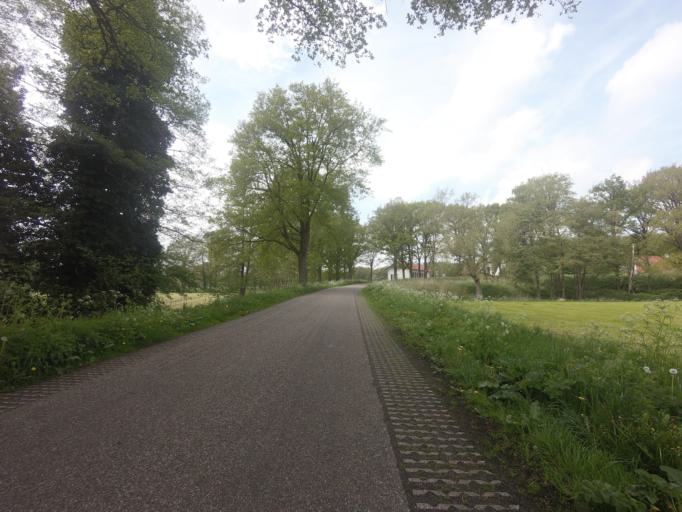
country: NL
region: Overijssel
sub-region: Gemeente Hof van Twente
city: Delden
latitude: 52.2452
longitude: 6.6791
